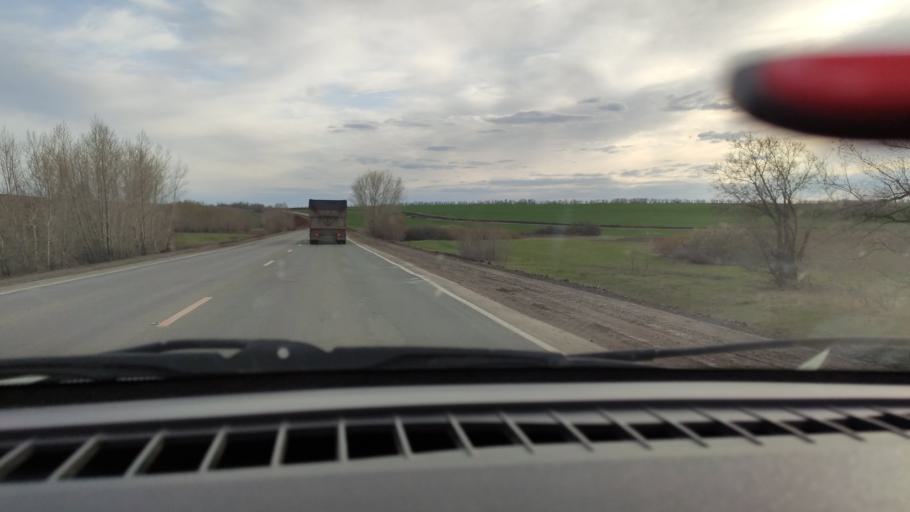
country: RU
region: Orenburg
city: Sakmara
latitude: 52.1908
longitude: 55.3008
